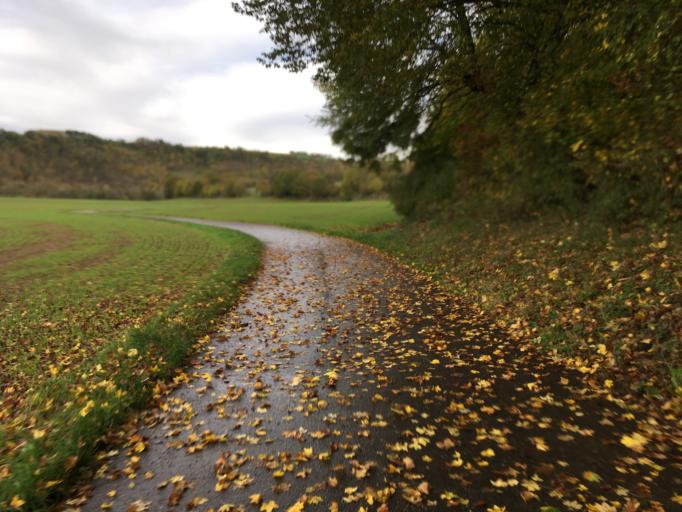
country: DE
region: Baden-Wuerttemberg
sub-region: Regierungsbezirk Stuttgart
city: Widdern
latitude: 49.3139
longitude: 9.3989
